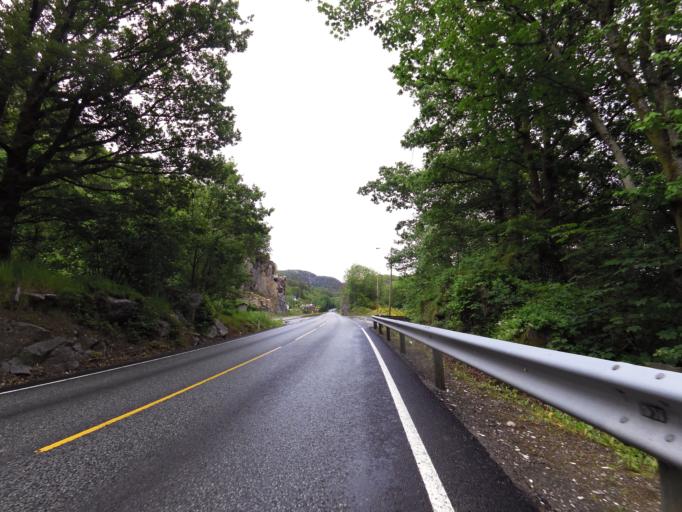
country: NO
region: Vest-Agder
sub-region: Farsund
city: Farsund
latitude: 58.1008
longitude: 6.8749
